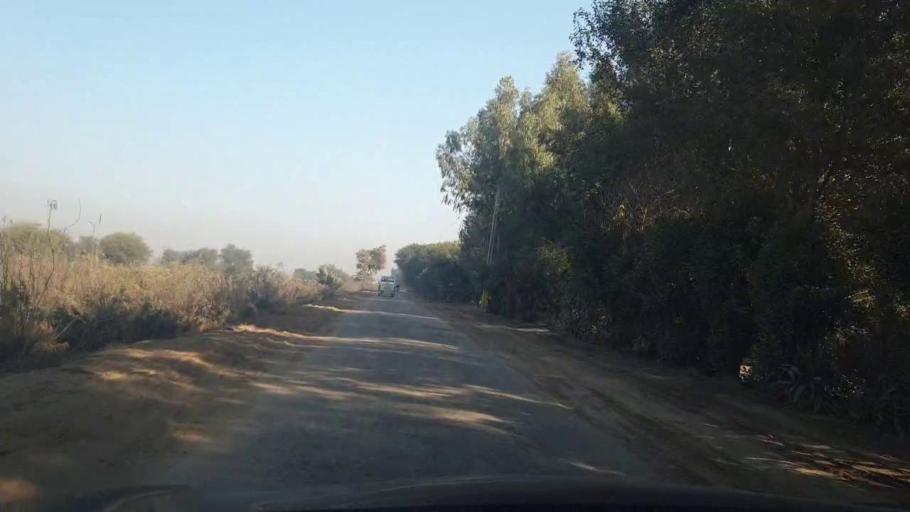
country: PK
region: Sindh
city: Mirpur Mathelo
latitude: 28.0667
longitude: 69.4656
